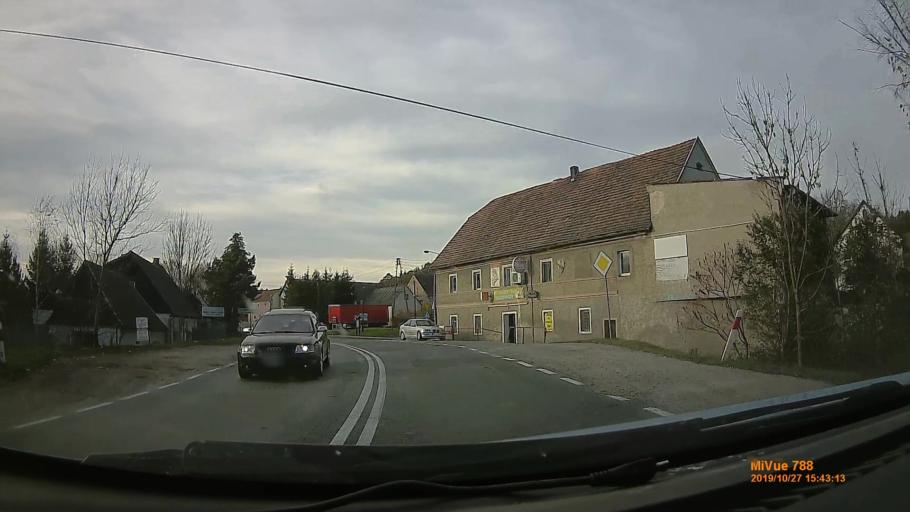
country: PL
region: Lower Silesian Voivodeship
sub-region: Powiat klodzki
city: Klodzko
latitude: 50.4672
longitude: 16.6215
